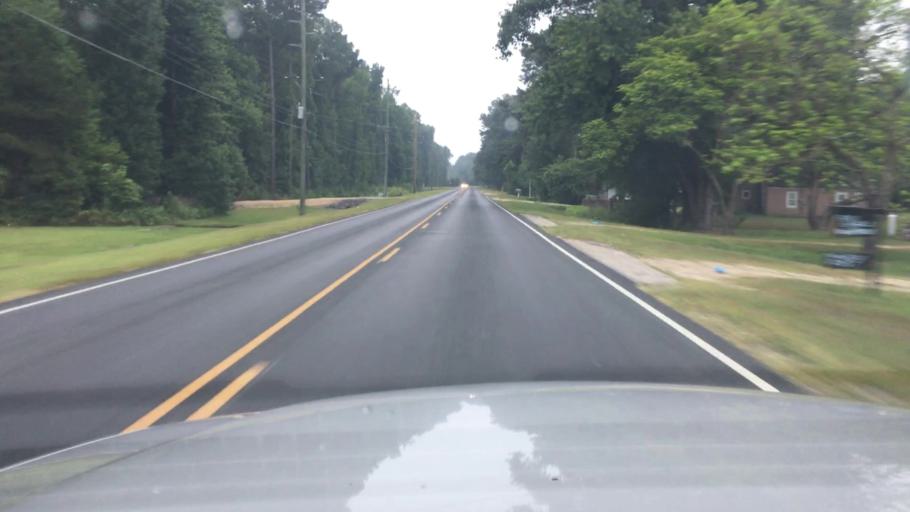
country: US
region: North Carolina
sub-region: Cumberland County
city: Fayetteville
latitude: 35.0065
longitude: -78.8625
